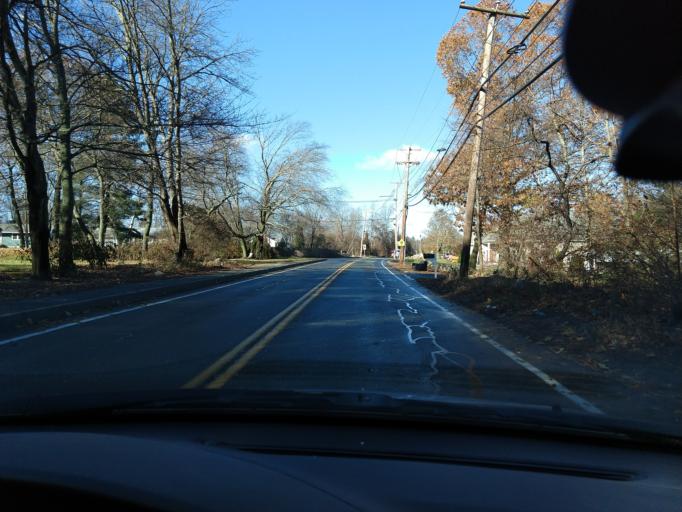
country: US
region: Massachusetts
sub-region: Middlesex County
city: Billerica
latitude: 42.5315
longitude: -71.2574
